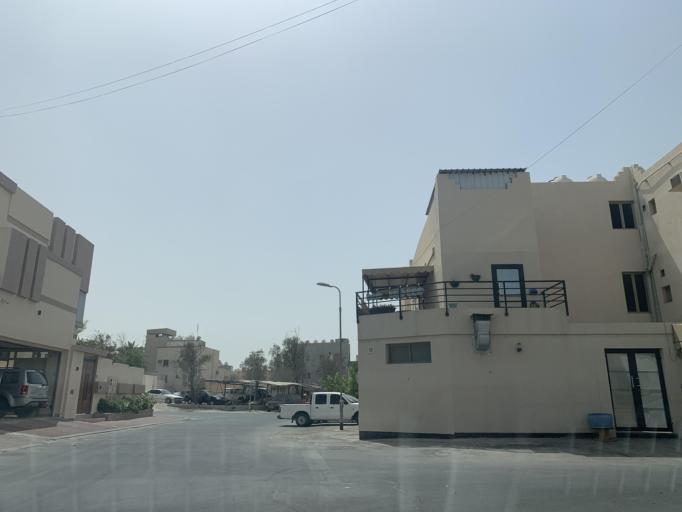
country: BH
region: Northern
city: Madinat `Isa
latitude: 26.1542
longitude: 50.5251
